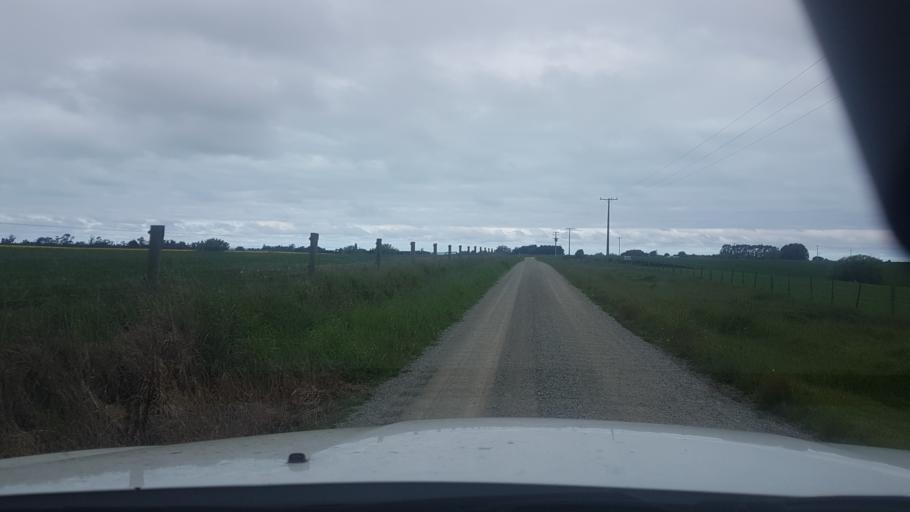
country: NZ
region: Canterbury
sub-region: Timaru District
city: Timaru
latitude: -44.4427
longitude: 171.2018
